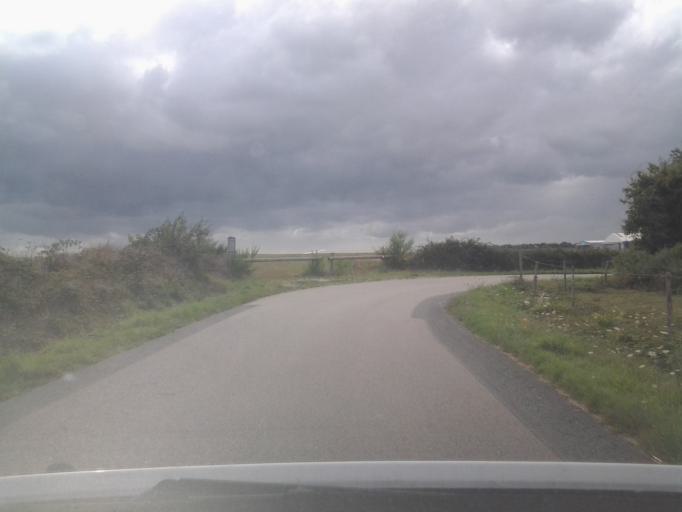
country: FR
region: Pays de la Loire
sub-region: Departement de la Vendee
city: Dompierre-sur-Yon
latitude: 46.7026
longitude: -1.3731
